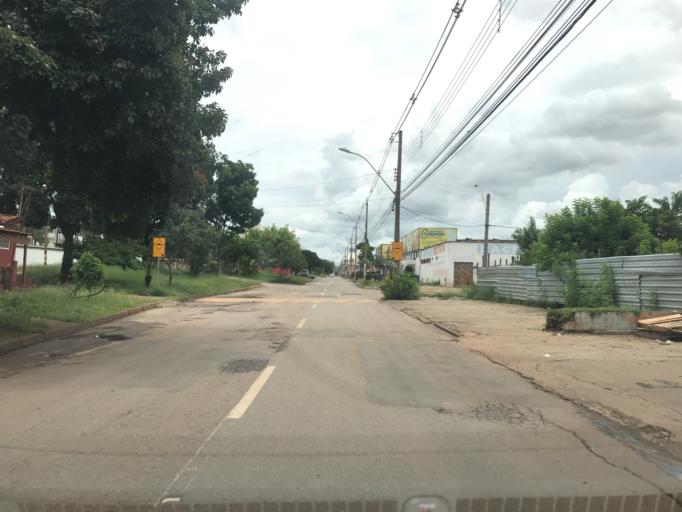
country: BR
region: Federal District
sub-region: Brasilia
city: Brasilia
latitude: -15.8193
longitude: -47.9558
